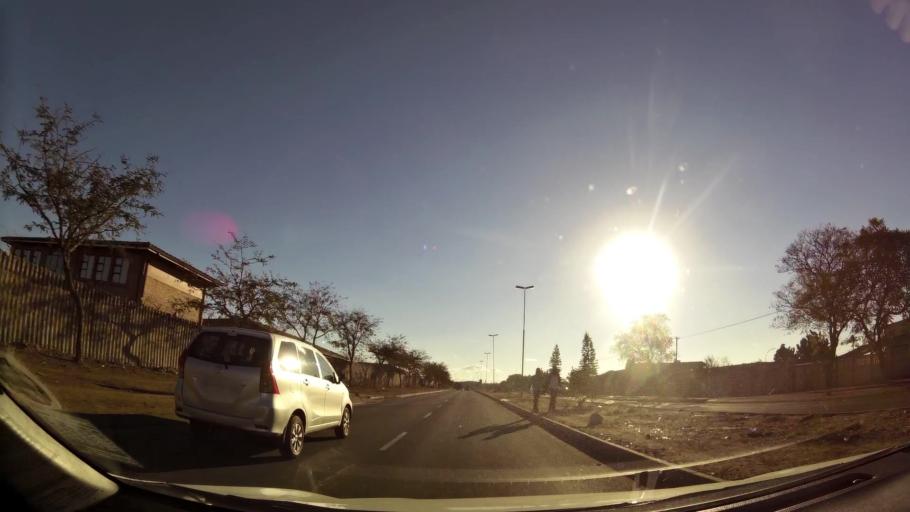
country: ZA
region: Limpopo
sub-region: Capricorn District Municipality
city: Polokwane
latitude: -23.8536
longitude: 29.3963
